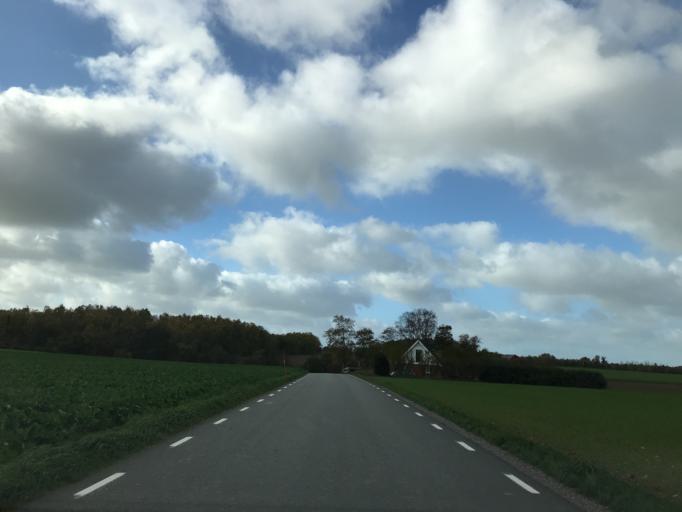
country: SE
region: Skane
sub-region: Bjuvs Kommun
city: Billesholm
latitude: 56.0113
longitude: 12.9877
